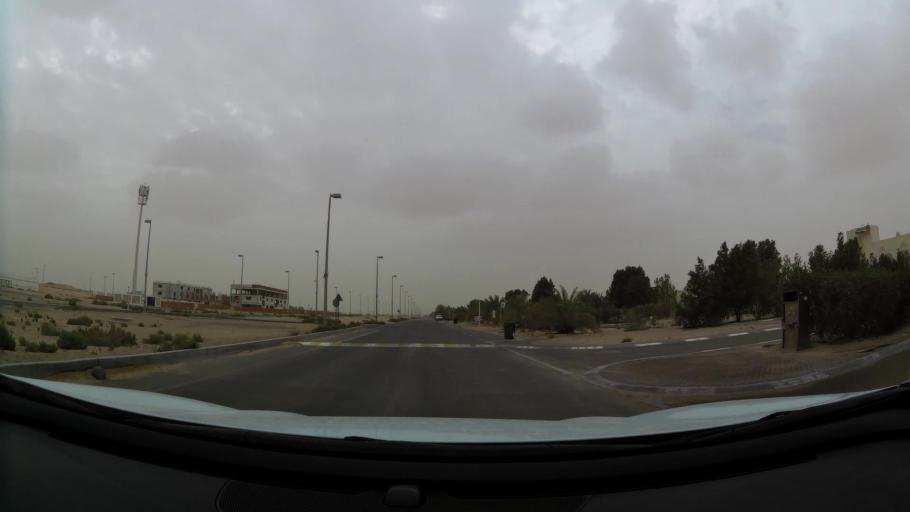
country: AE
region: Abu Dhabi
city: Abu Dhabi
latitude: 24.4262
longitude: 54.7270
